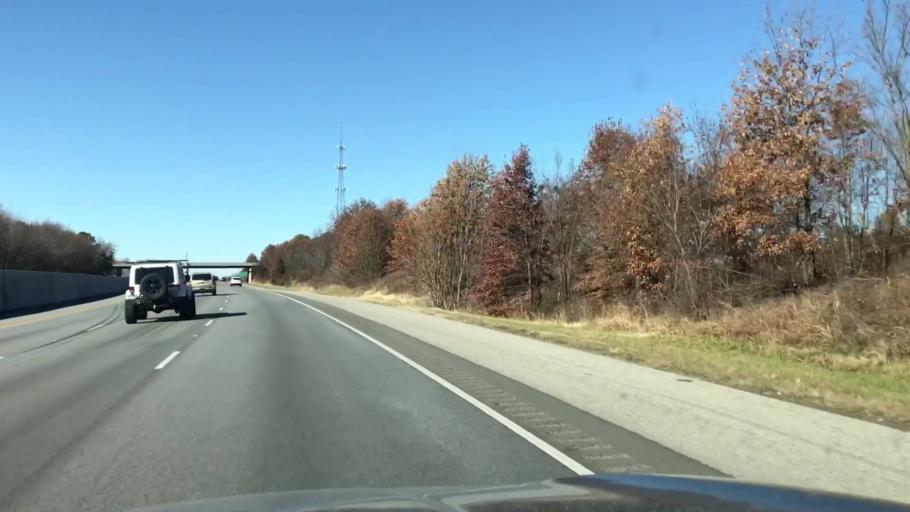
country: US
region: Arkansas
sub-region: Benton County
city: Lowell
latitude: 36.2960
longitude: -94.1677
